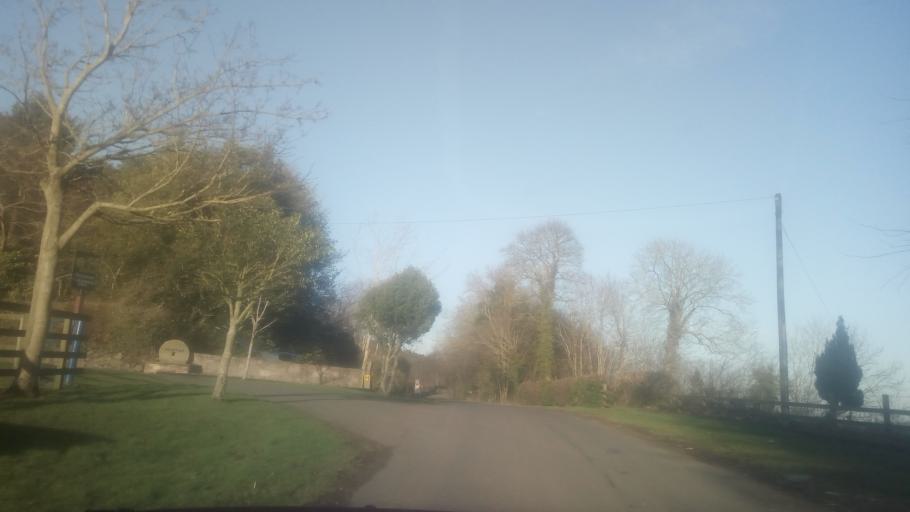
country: GB
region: Scotland
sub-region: The Scottish Borders
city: Saint Boswells
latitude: 55.4709
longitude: -2.6684
